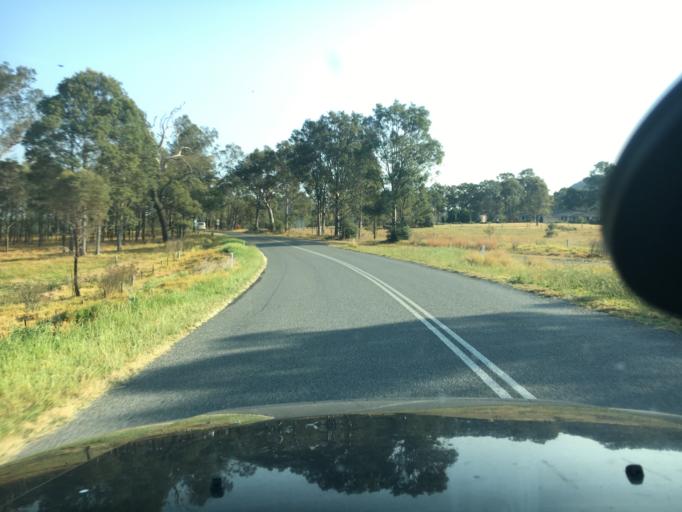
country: AU
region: New South Wales
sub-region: Cessnock
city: Branxton
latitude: -32.5922
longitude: 151.3324
